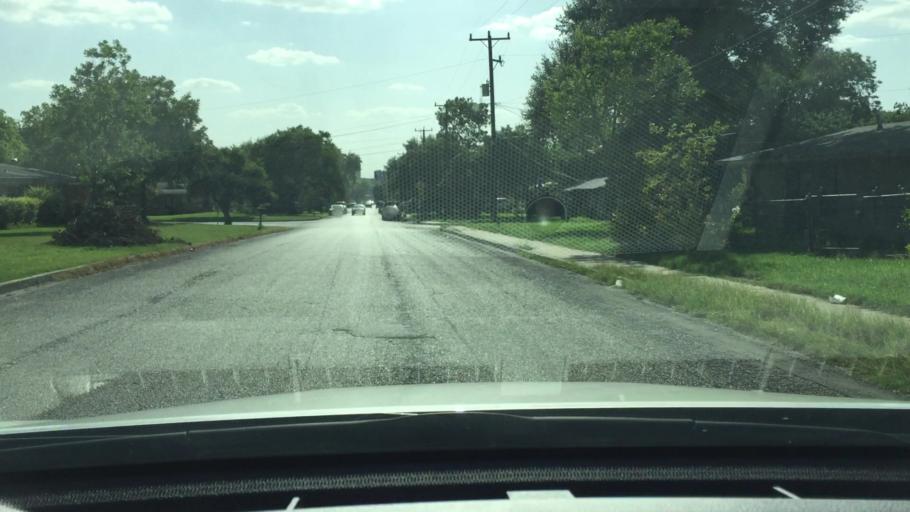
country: US
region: Texas
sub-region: Bexar County
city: Windcrest
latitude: 29.5327
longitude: -98.3848
